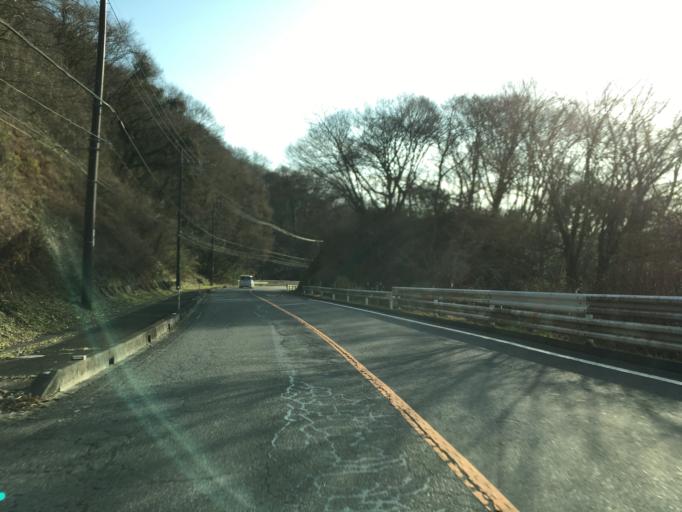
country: JP
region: Ibaraki
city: Daigo
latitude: 36.7528
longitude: 140.4015
